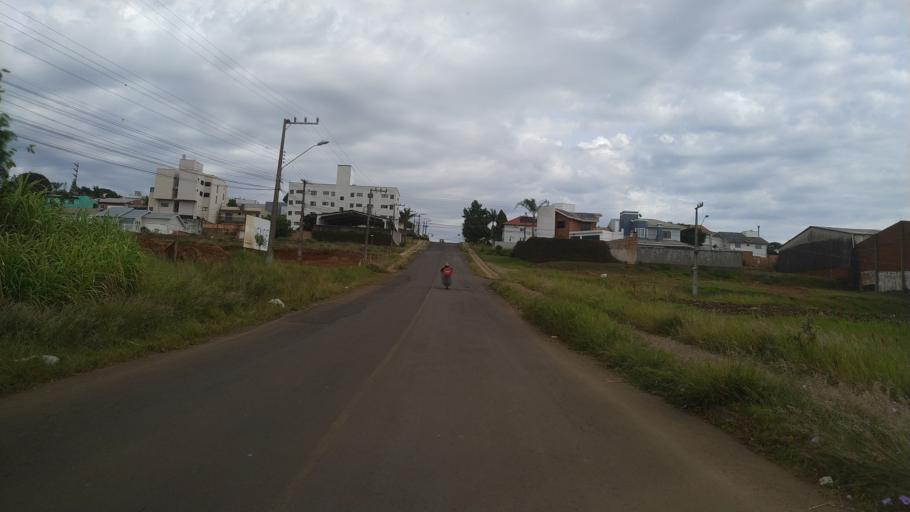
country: BR
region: Santa Catarina
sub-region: Chapeco
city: Chapeco
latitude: -27.1012
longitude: -52.5981
